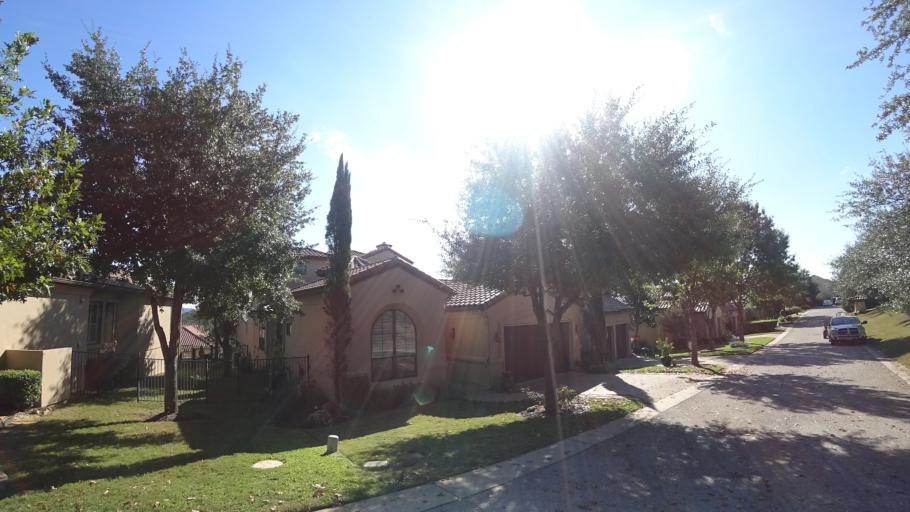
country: US
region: Texas
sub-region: Travis County
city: Hudson Bend
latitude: 30.3616
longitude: -97.8873
